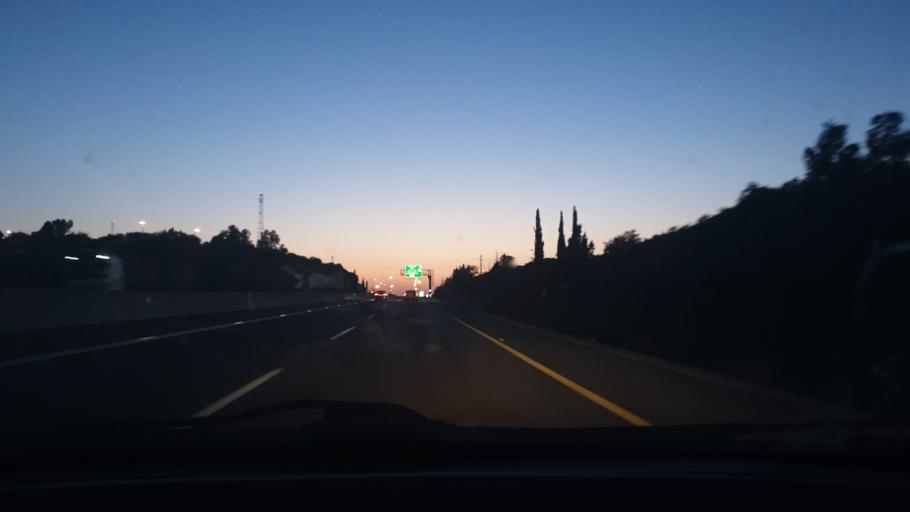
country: IL
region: Central District
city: Gedera
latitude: 31.7990
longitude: 34.7790
